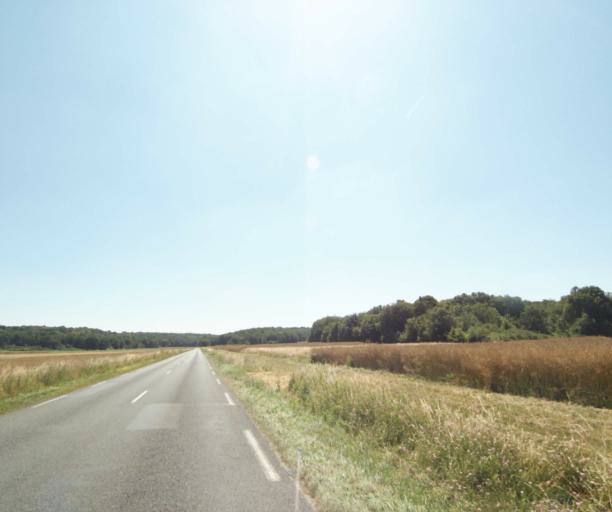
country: FR
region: Ile-de-France
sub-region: Departement de l'Essonne
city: Milly-la-Foret
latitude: 48.3731
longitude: 2.4733
